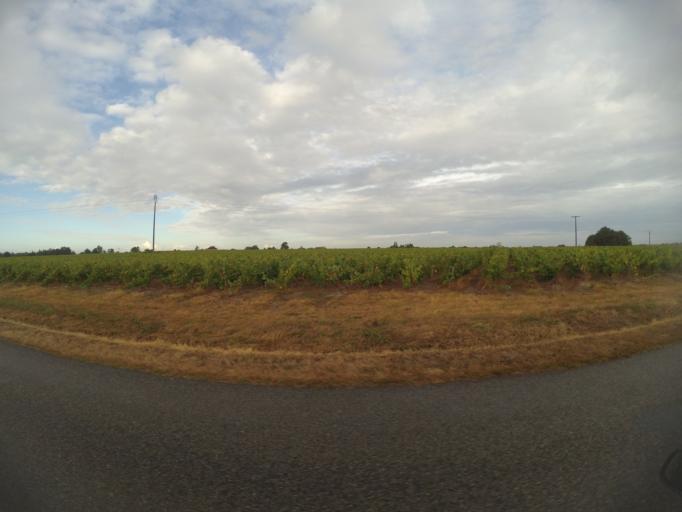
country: FR
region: Pays de la Loire
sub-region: Departement de la Loire-Atlantique
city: Aigrefeuille-sur-Maine
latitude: 47.0592
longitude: -1.4121
